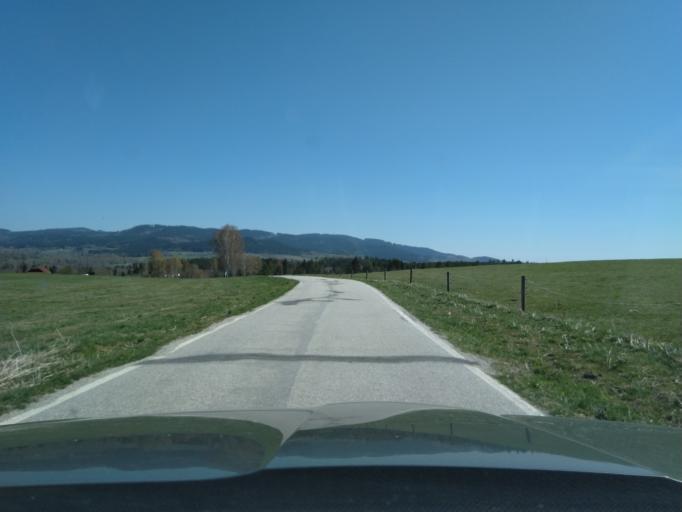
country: CZ
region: Jihocesky
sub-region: Okres Cesky Krumlov
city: Horni Plana
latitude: 48.7795
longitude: 13.9375
